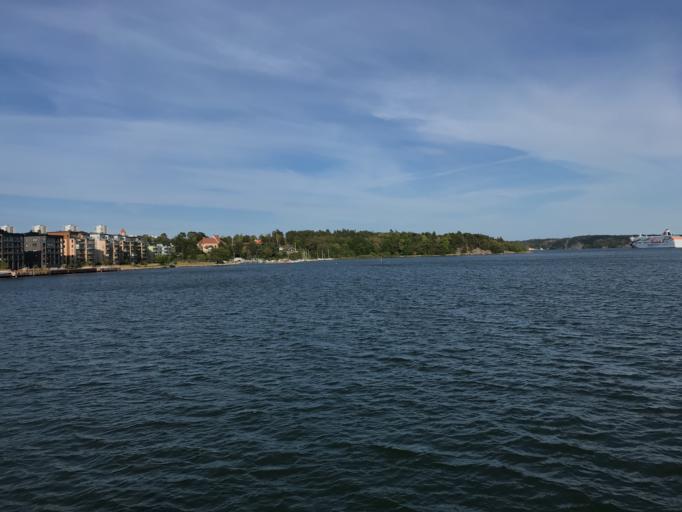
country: SE
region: Stockholm
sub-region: Lidingo
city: Lidingoe
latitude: 59.3415
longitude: 18.1522
